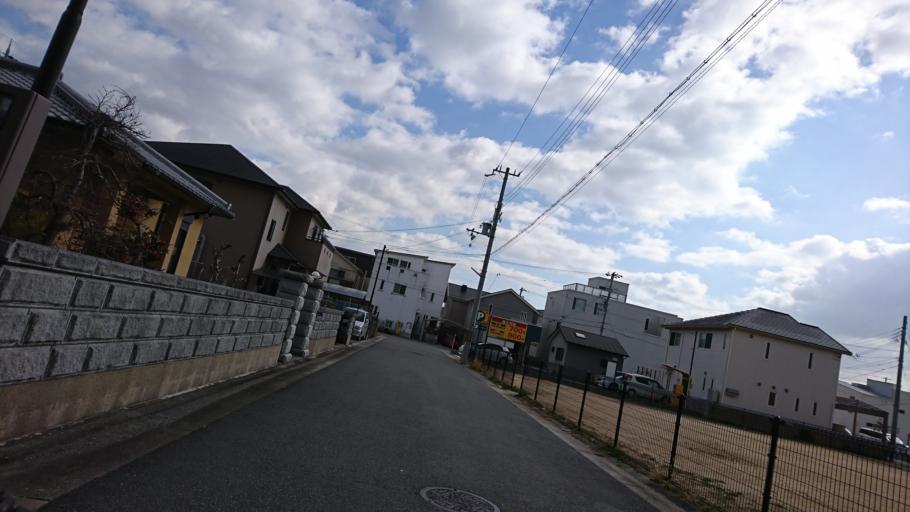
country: JP
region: Hyogo
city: Kakogawacho-honmachi
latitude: 34.7676
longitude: 134.8424
